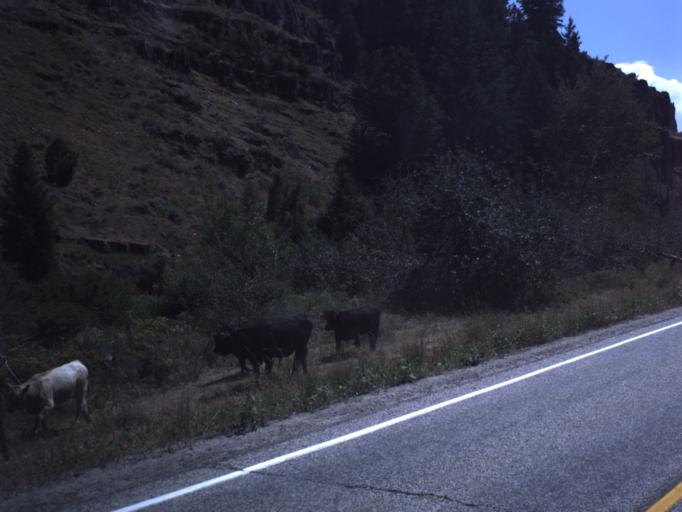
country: US
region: Utah
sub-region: Cache County
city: North Logan
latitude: 41.8551
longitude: -111.5862
